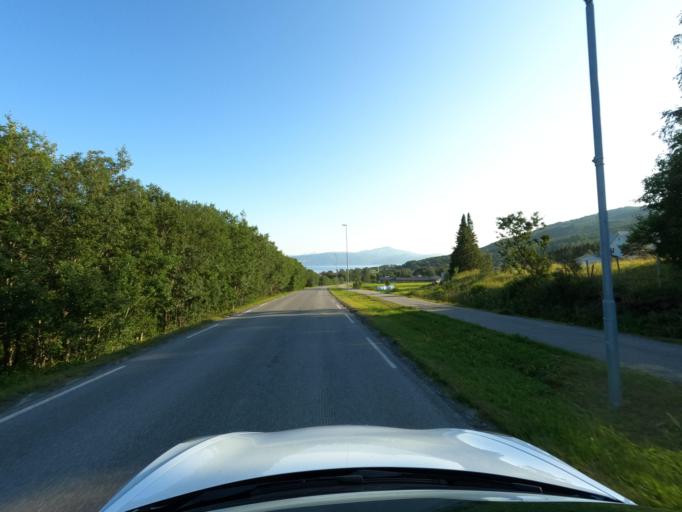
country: NO
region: Nordland
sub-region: Evenes
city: Randa
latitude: 68.4862
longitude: 16.8971
